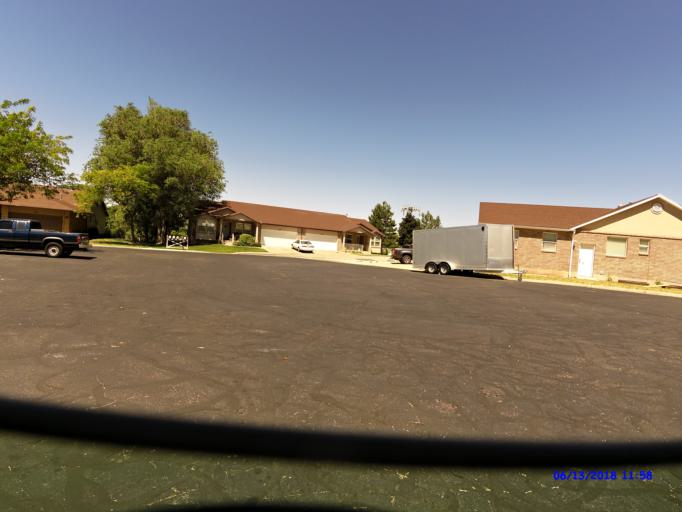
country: US
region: Utah
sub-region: Weber County
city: Ogden
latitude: 41.2322
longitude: -111.9454
